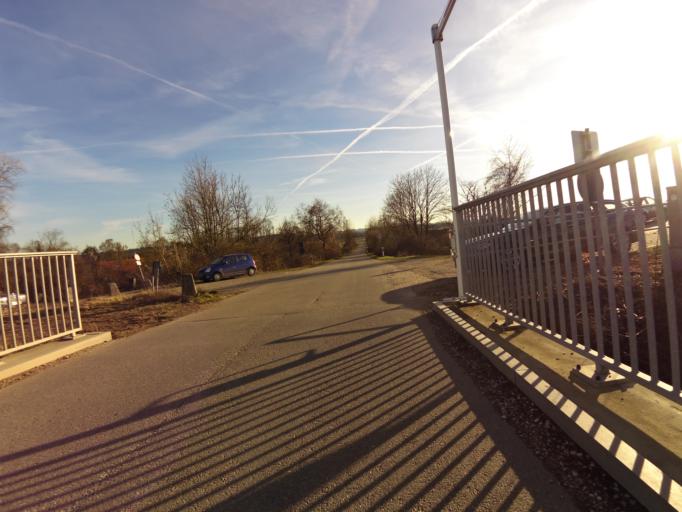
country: DE
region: Bavaria
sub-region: Upper Bavaria
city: Wang
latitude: 48.4904
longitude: 11.9874
